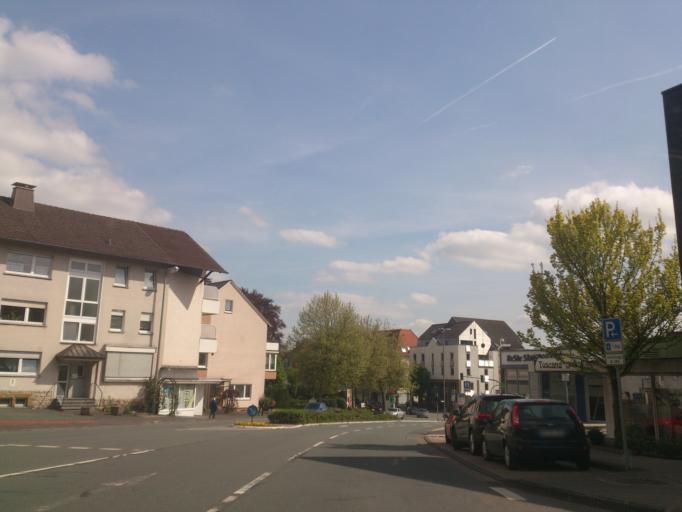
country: DE
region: North Rhine-Westphalia
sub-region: Regierungsbezirk Detmold
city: Bad Driburg
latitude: 51.7350
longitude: 9.0228
